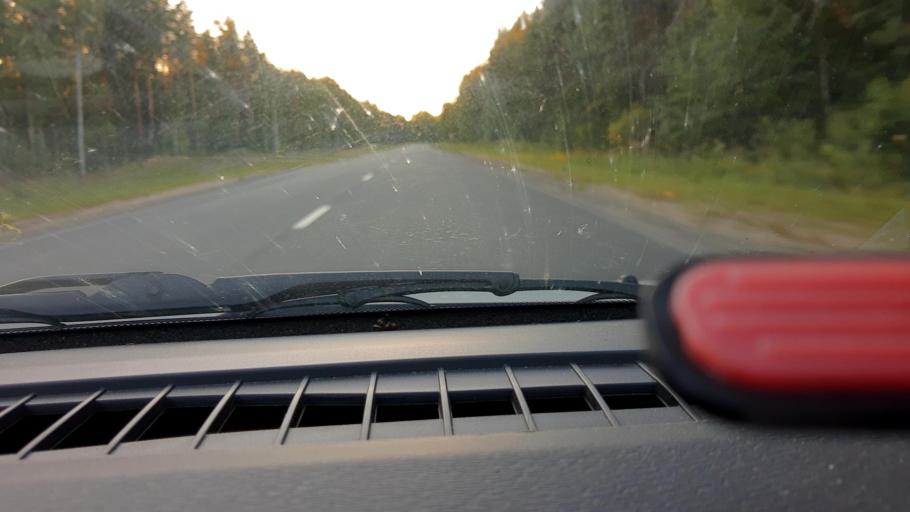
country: RU
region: Nizjnij Novgorod
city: Uren'
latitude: 57.3820
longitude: 45.6887
